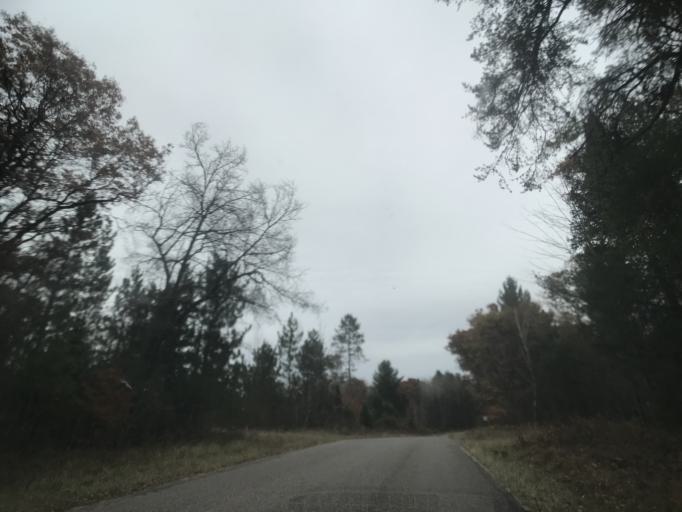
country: US
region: Wisconsin
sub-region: Oconto County
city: Gillett
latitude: 45.3750
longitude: -88.3205
